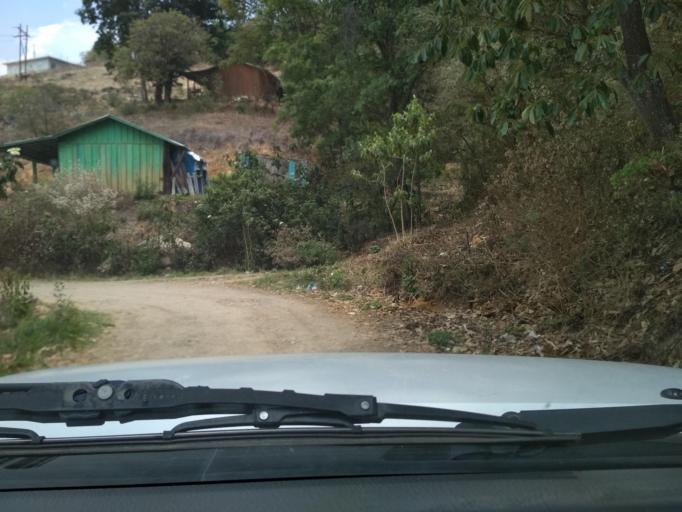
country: MX
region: Veracruz
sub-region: Acultzingo
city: Acatla
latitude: 18.7504
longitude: -97.1918
